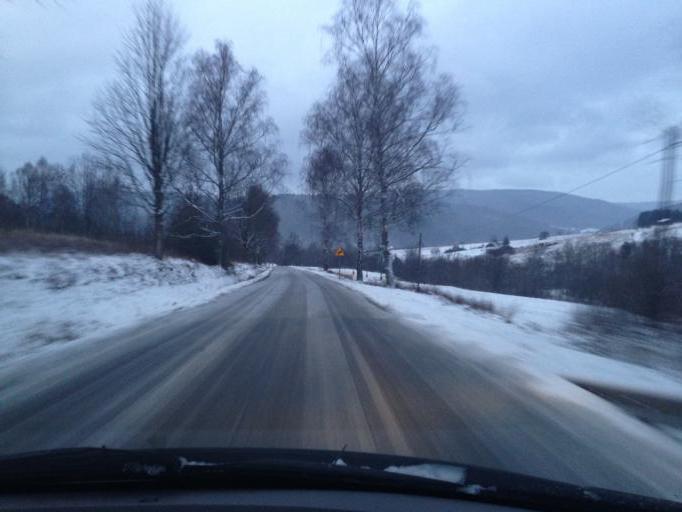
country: PL
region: Subcarpathian Voivodeship
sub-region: Powiat jasielski
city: Krempna
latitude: 49.5221
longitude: 21.5020
